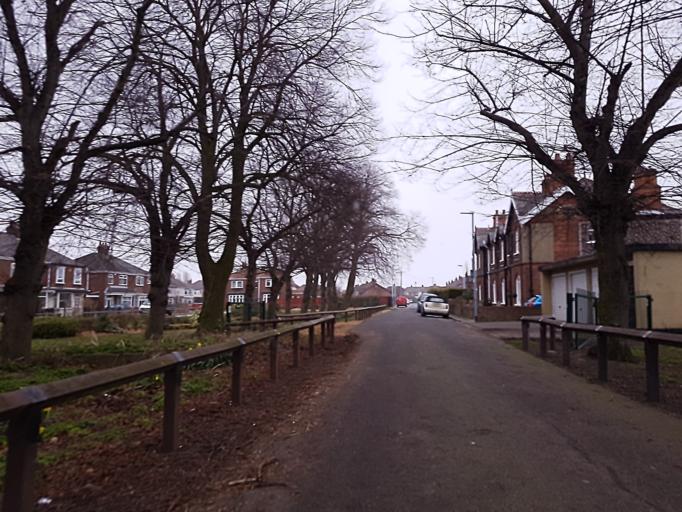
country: GB
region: England
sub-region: North East Lincolnshire
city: Grimbsy
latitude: 53.5601
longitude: -0.1089
